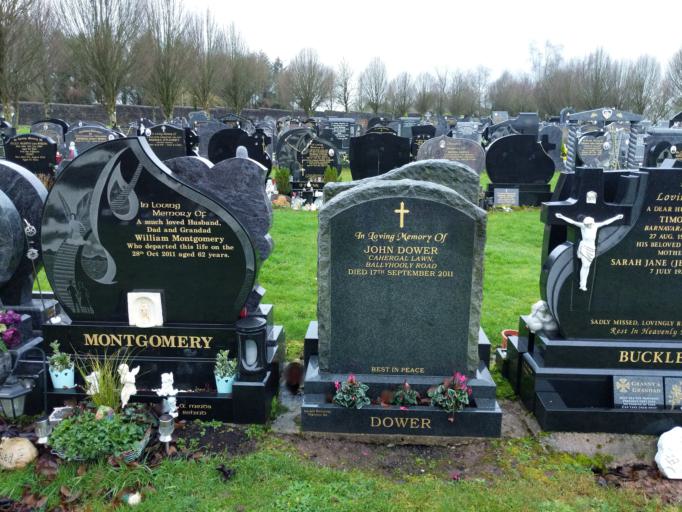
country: IE
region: Munster
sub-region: County Cork
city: Cork
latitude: 51.9383
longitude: -8.4729
